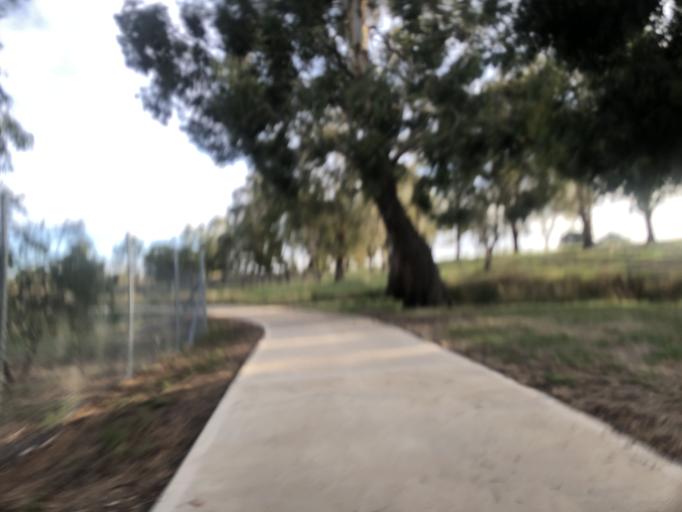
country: AU
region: New South Wales
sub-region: Orange Municipality
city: Orange
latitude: -33.3007
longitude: 149.0921
